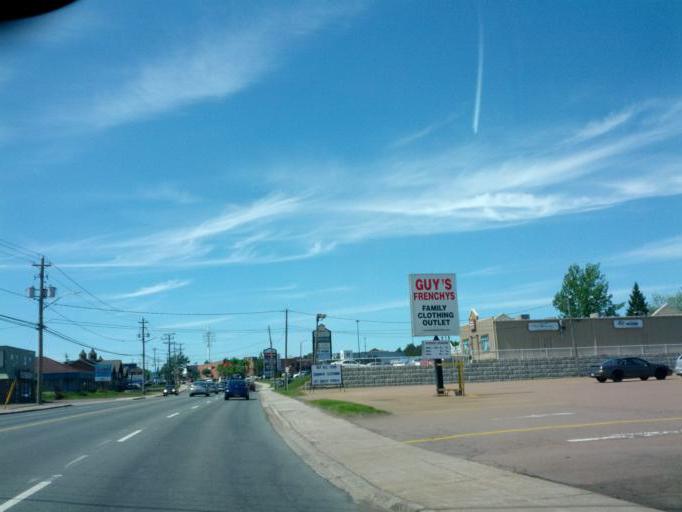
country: CA
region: New Brunswick
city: Moncton
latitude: 46.1155
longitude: -64.8387
